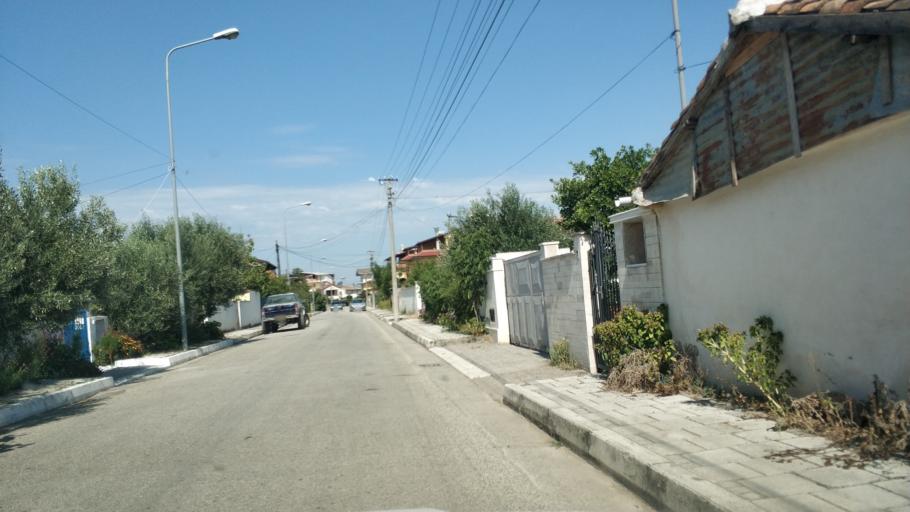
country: AL
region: Fier
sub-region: Rrethi i Lushnjes
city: Divjake
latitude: 40.9970
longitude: 19.5280
